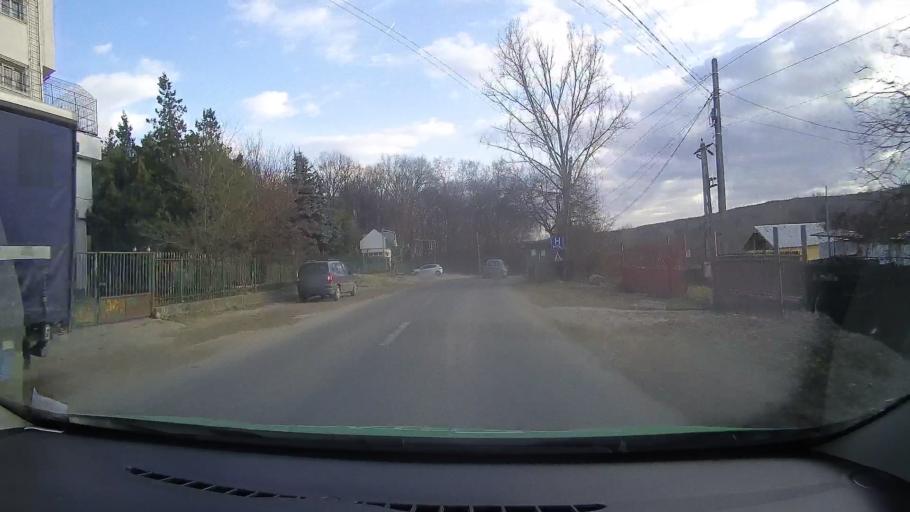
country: RO
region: Dambovita
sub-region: Comuna Gura Ocnitei
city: Gura Ocnitei
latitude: 44.9586
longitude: 25.5504
